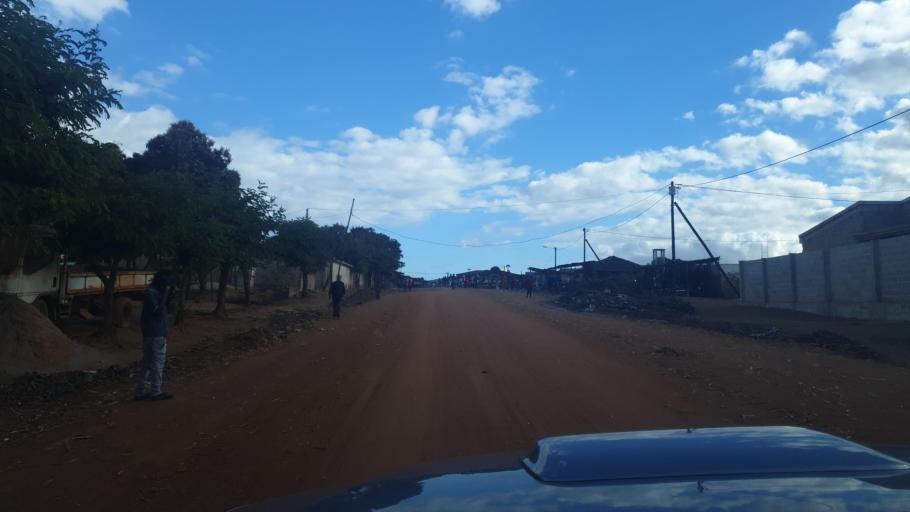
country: MZ
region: Nampula
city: Nampula
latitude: -15.1012
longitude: 39.2218
